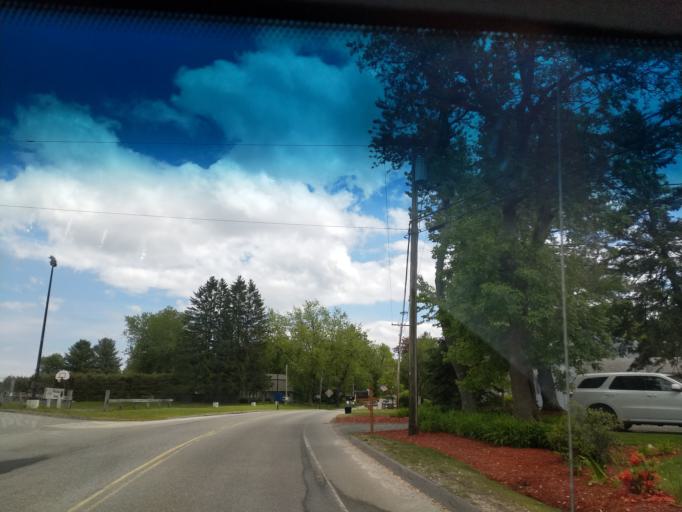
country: US
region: Maine
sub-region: Cumberland County
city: Falmouth
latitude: 43.7462
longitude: -70.2943
